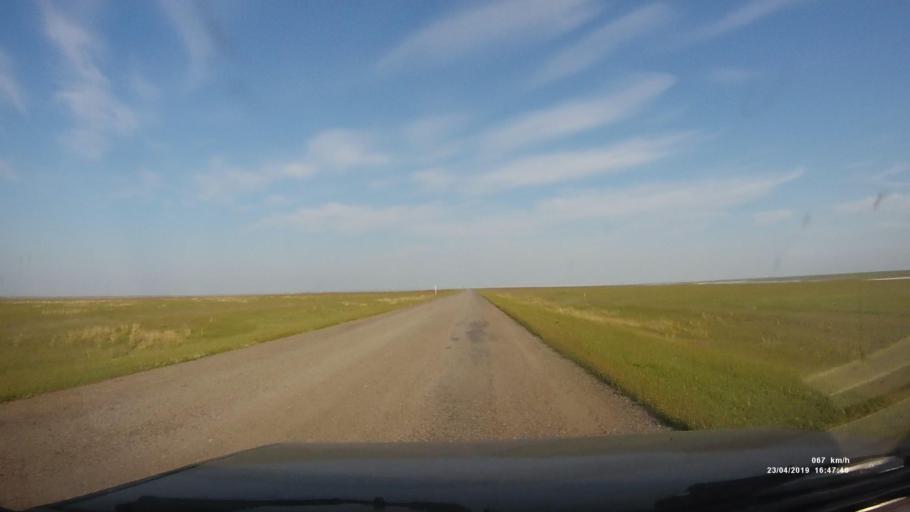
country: RU
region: Kalmykiya
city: Priyutnoye
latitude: 46.3380
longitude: 43.2509
